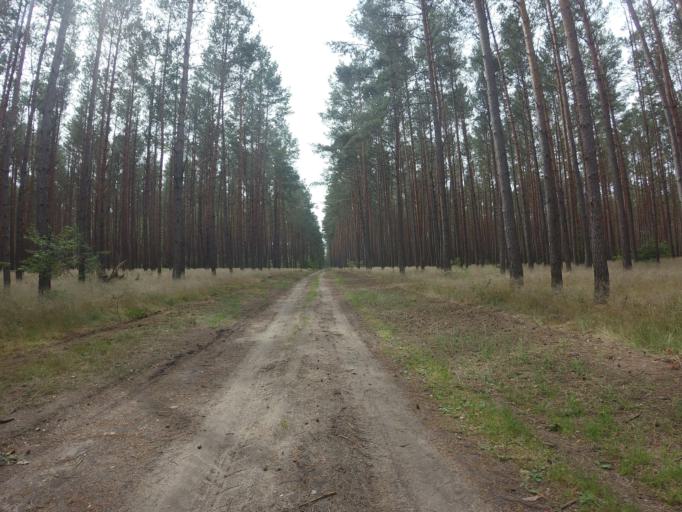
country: PL
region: West Pomeranian Voivodeship
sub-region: Powiat choszczenski
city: Bierzwnik
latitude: 53.1265
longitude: 15.6866
